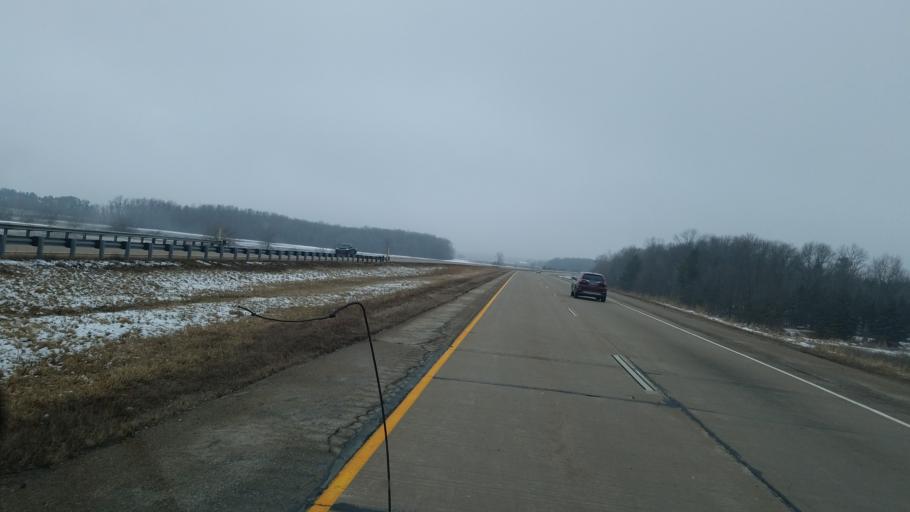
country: US
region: Wisconsin
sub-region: Winnebago County
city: Winneconne
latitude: 44.2342
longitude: -88.7658
